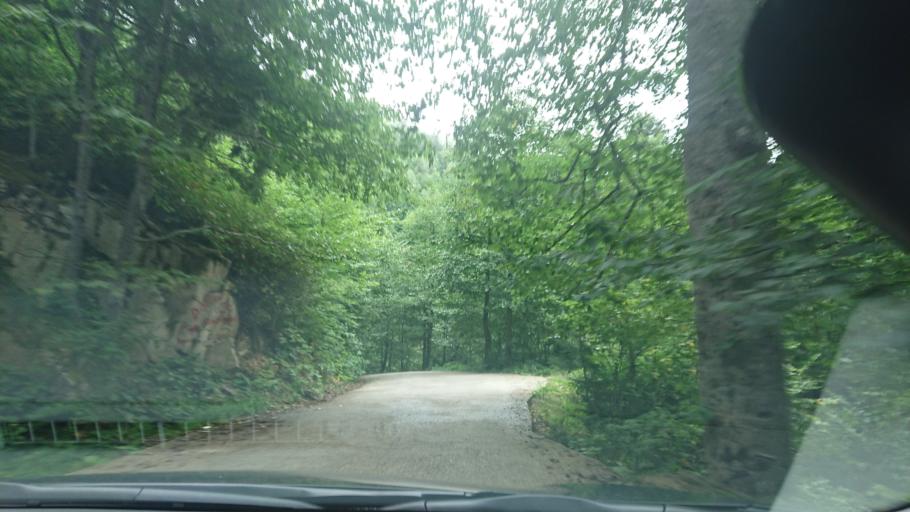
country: TR
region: Gumushane
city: Kurtun
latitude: 40.6692
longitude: 39.0392
